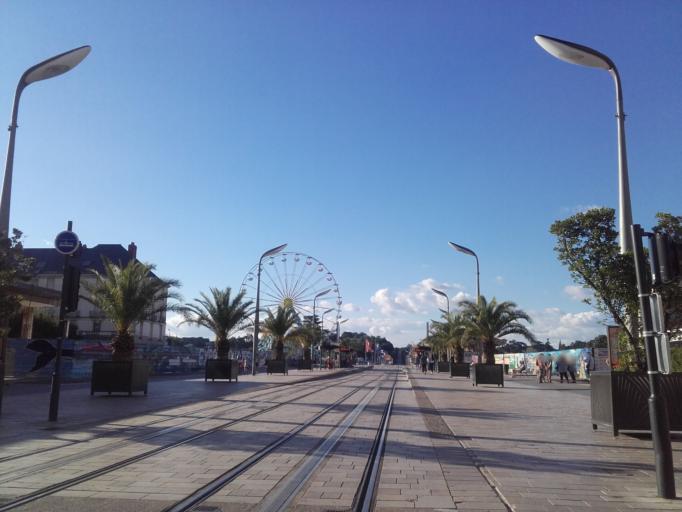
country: FR
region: Centre
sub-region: Departement d'Indre-et-Loire
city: Tours
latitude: 47.3954
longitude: 0.6867
